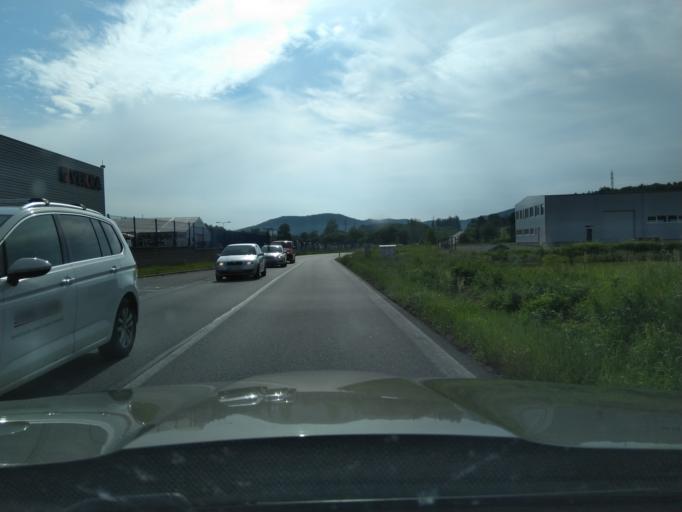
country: CZ
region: Jihocesky
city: Husinec
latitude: 49.0518
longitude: 14.0015
